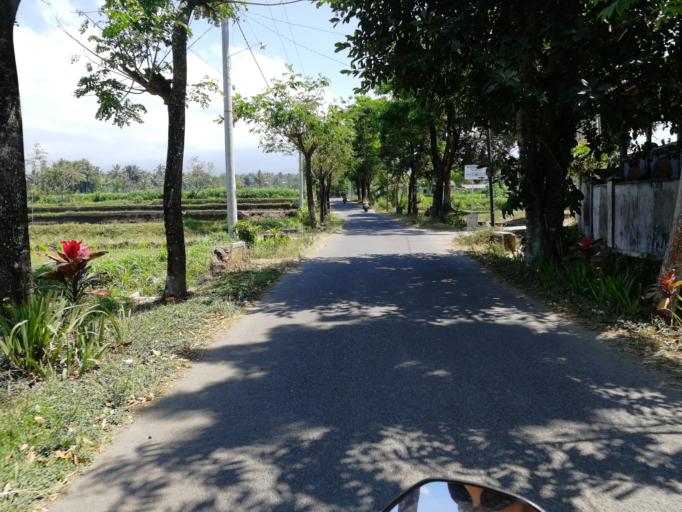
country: ID
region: West Nusa Tenggara
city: Tetebatu
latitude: -8.5580
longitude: 116.4195
